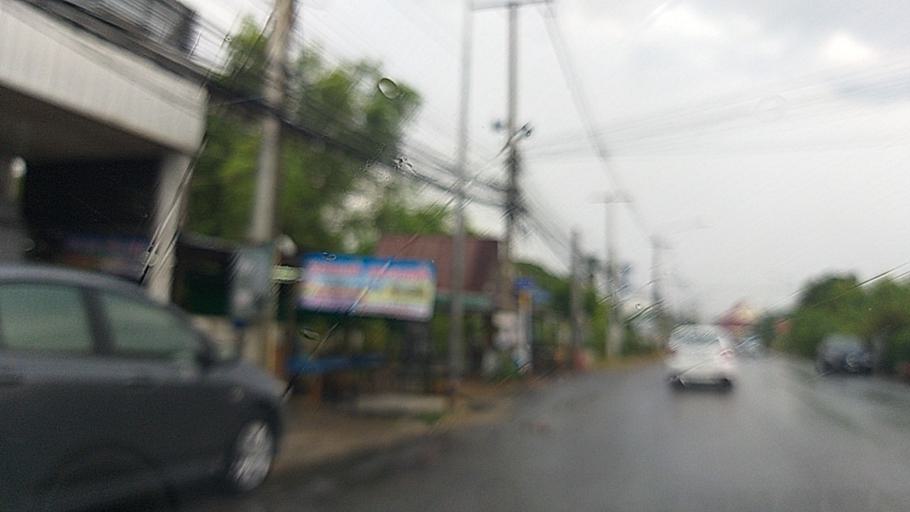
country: TH
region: Phra Nakhon Si Ayutthaya
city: Phra Nakhon Si Ayutthaya
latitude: 14.3494
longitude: 100.5428
